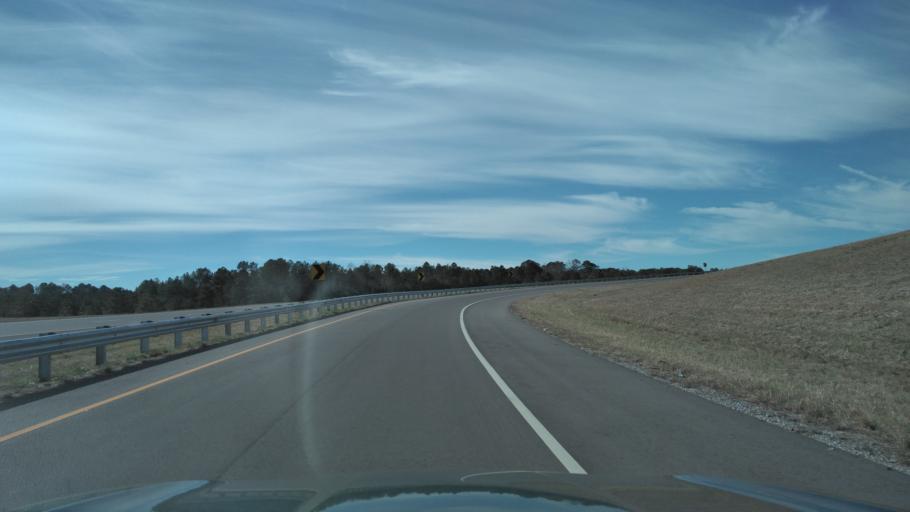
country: US
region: Alabama
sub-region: Walker County
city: Jasper
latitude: 33.8541
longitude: -87.3480
